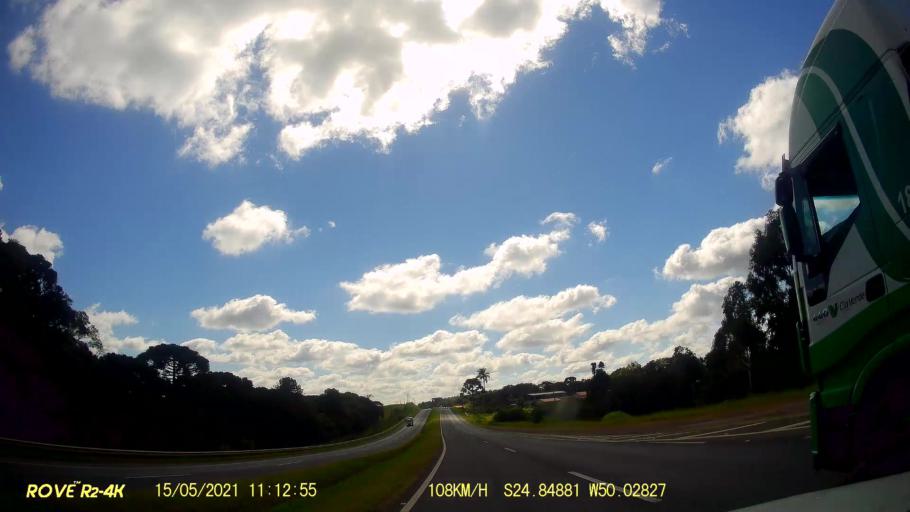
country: BR
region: Parana
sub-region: Castro
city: Castro
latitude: -24.8490
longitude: -50.0285
